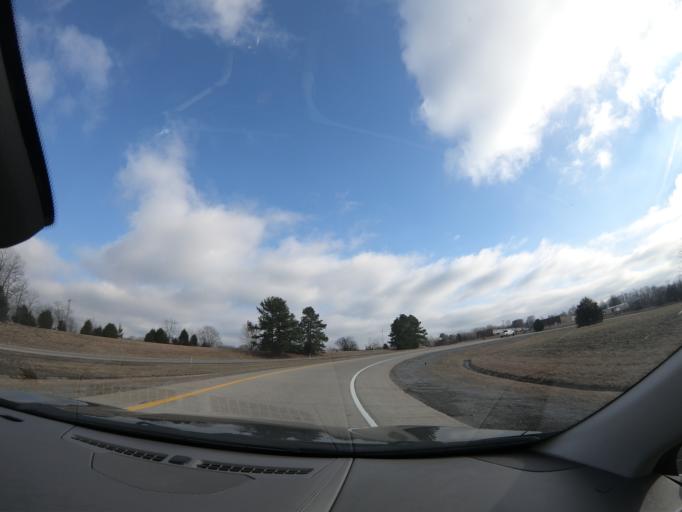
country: US
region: Tennessee
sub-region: Sumner County
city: Millersville
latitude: 36.4184
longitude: -86.7155
